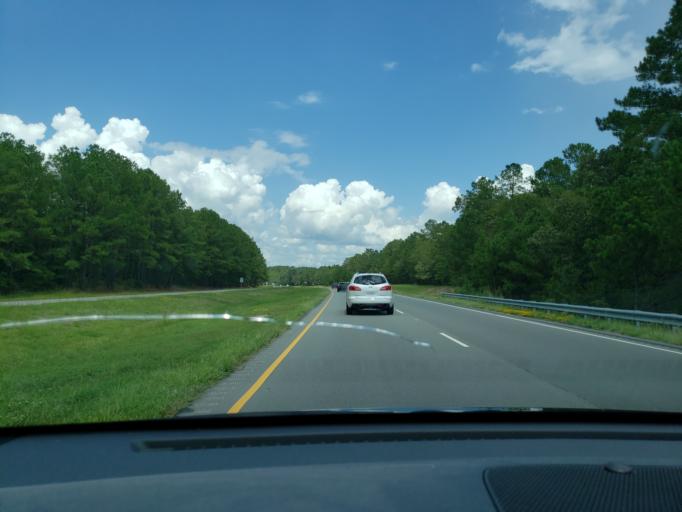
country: US
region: North Carolina
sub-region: Robeson County
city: Saint Pauls
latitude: 34.8522
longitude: -78.8510
